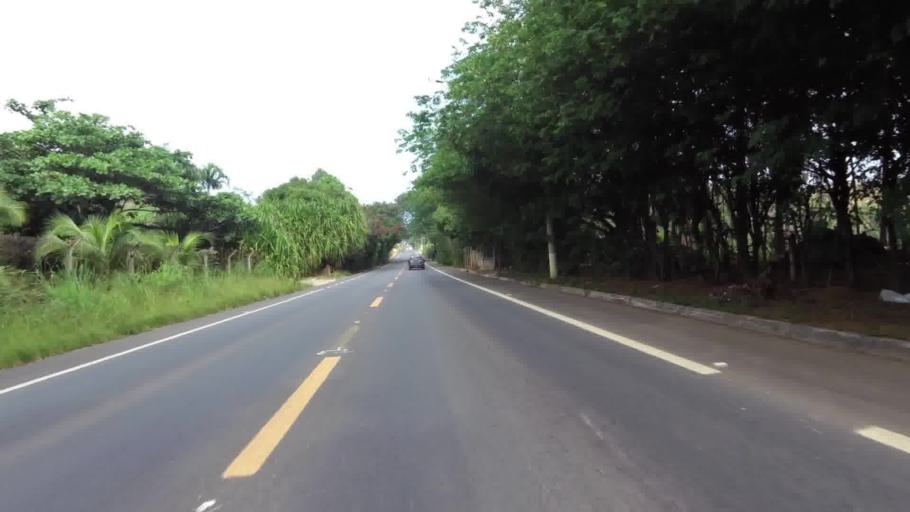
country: BR
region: Espirito Santo
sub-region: Piuma
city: Piuma
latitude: -20.8084
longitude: -40.6793
